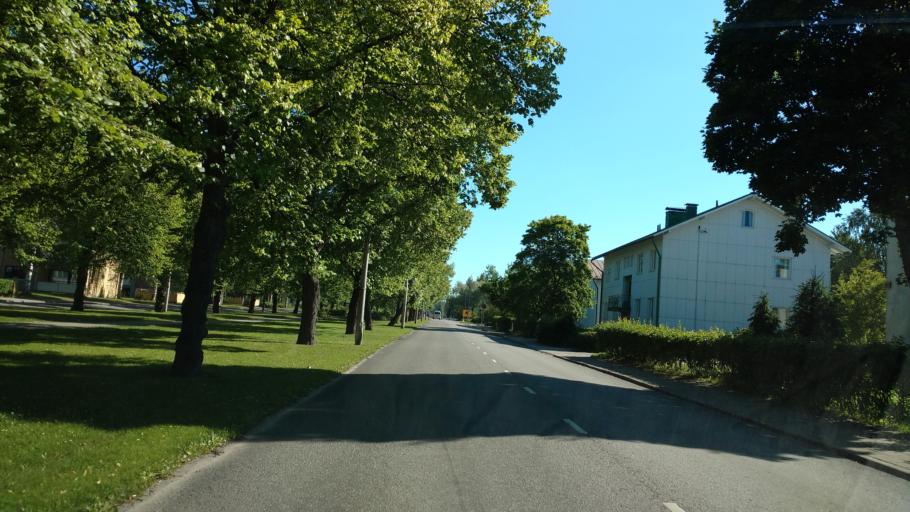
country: FI
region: Varsinais-Suomi
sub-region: Salo
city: Salo
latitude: 60.3891
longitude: 23.1419
